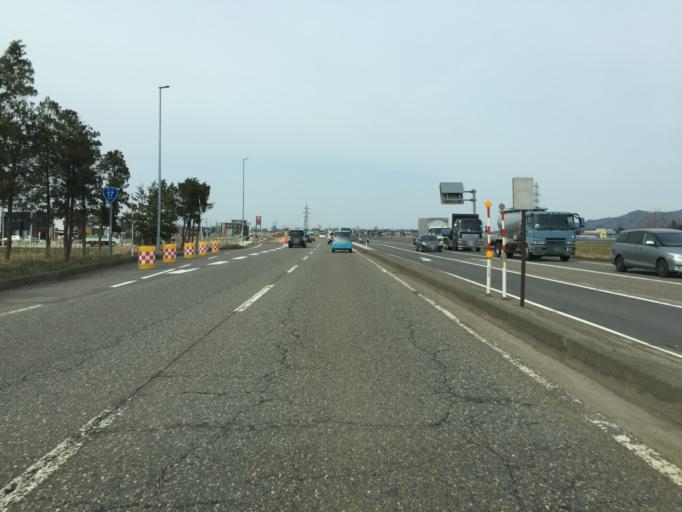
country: JP
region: Niigata
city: Nagaoka
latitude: 37.4258
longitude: 138.8636
